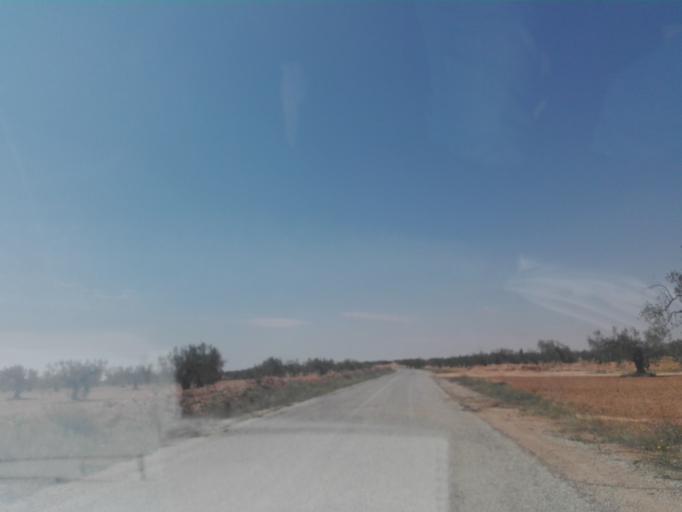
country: TN
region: Safaqis
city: Bi'r `Ali Bin Khalifah
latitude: 34.6486
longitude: 10.4124
